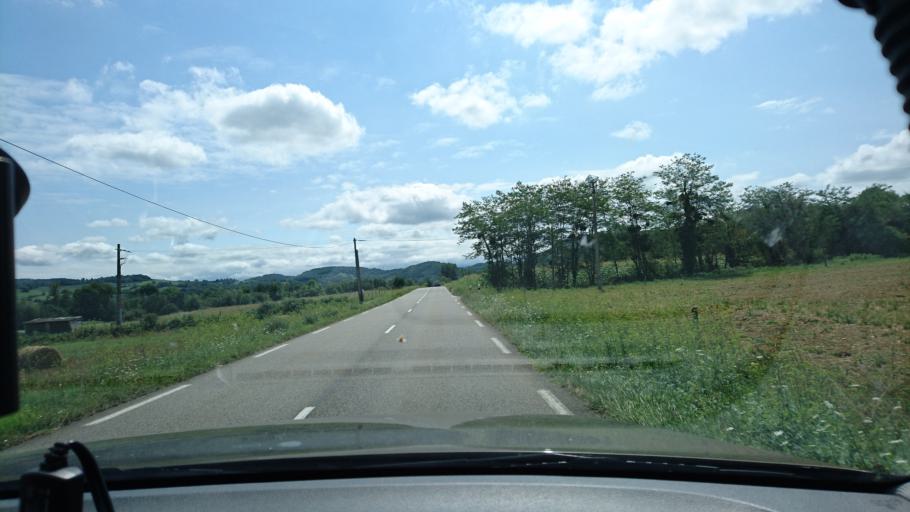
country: FR
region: Midi-Pyrenees
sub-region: Departement de la Haute-Garonne
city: Gaillac-Toulza
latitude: 43.1227
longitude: 1.4415
